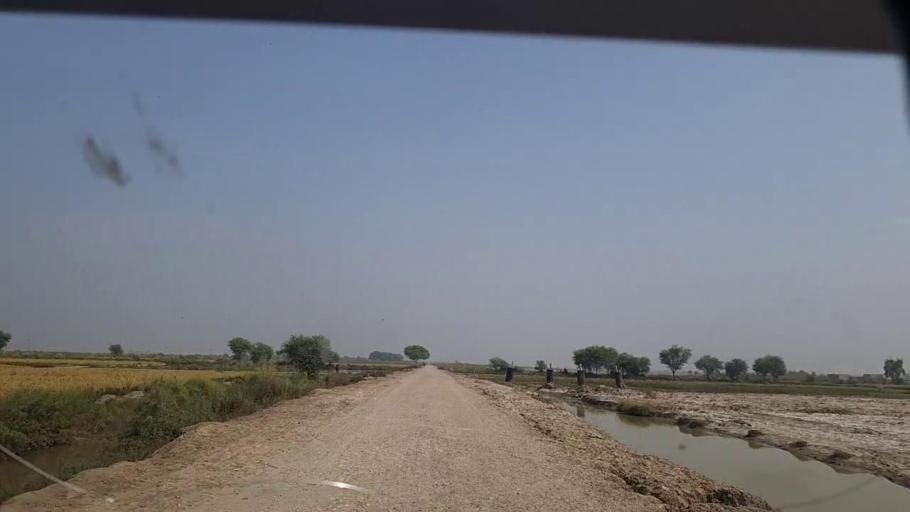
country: PK
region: Sindh
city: Shikarpur
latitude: 28.0362
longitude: 68.6355
